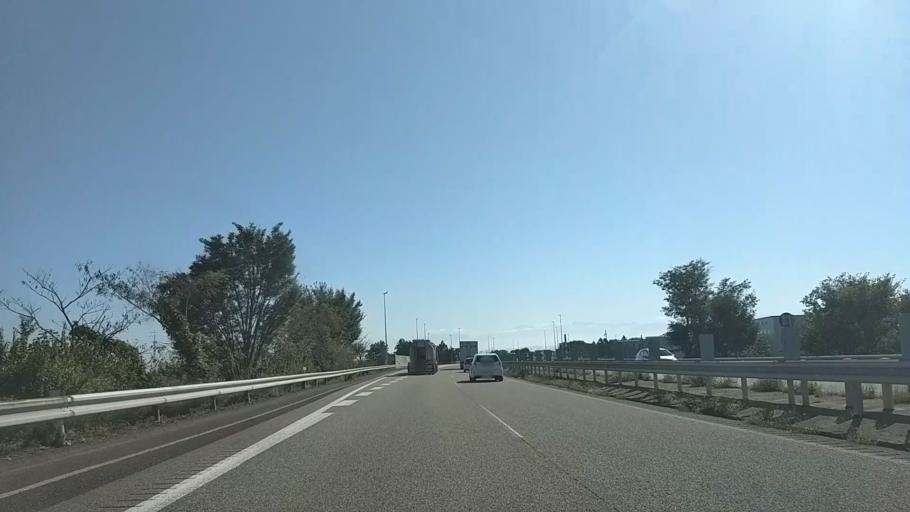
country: JP
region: Toyama
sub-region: Oyabe Shi
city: Oyabe
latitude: 36.6302
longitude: 136.8450
